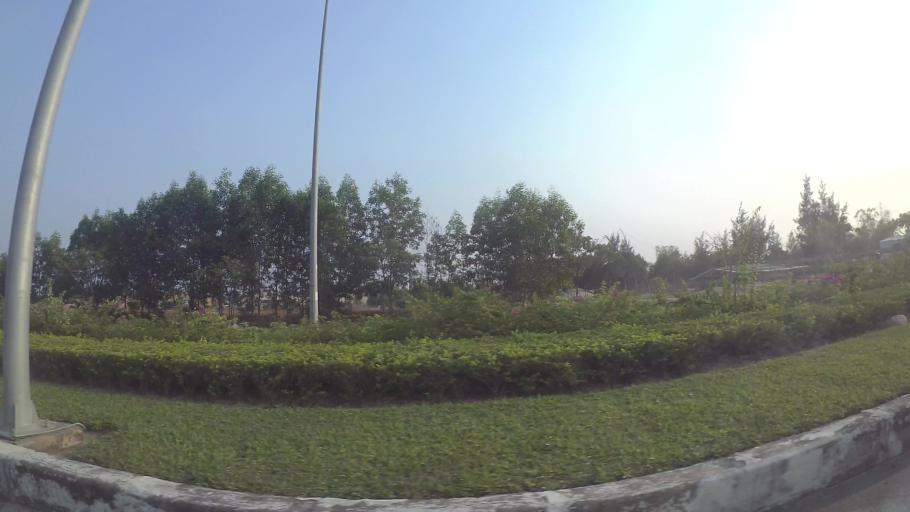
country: VN
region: Da Nang
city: Ngu Hanh Son
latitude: 15.9779
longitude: 108.2412
